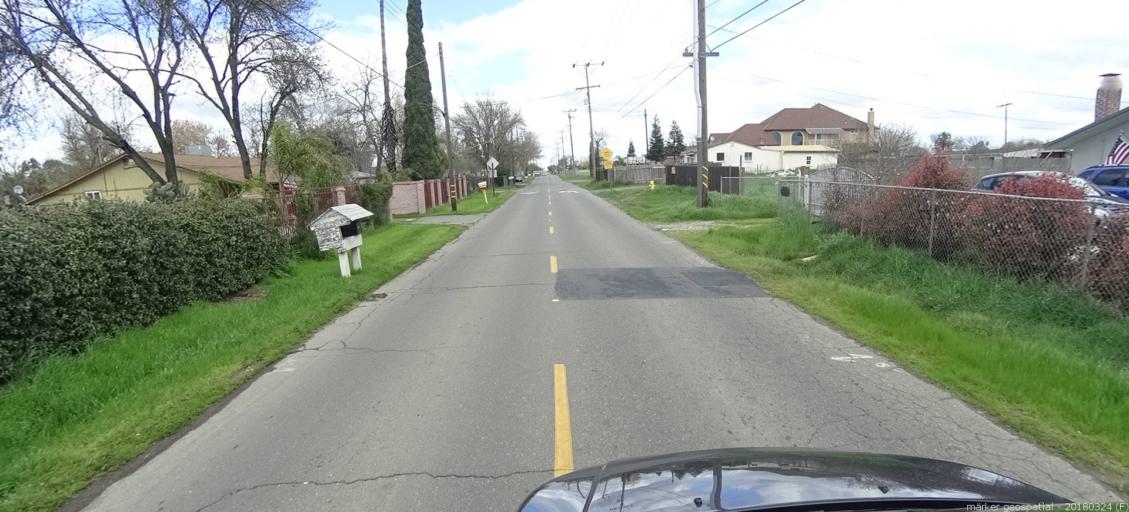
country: US
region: California
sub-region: Sacramento County
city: North Highlands
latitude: 38.6783
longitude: -121.3875
